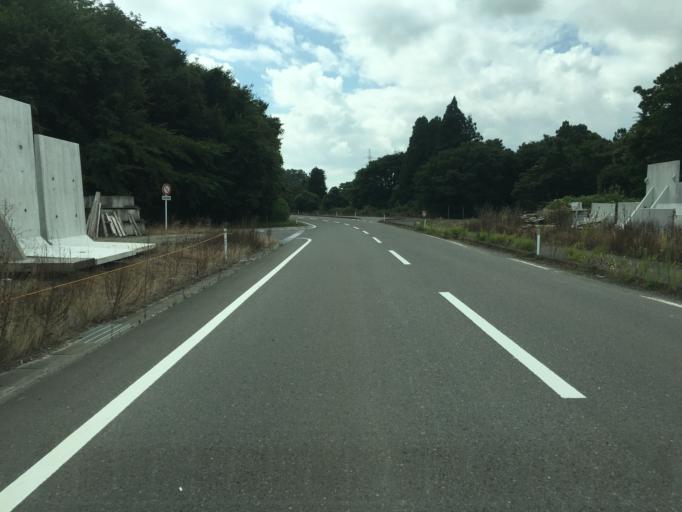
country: JP
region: Fukushima
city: Motomiya
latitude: 37.4780
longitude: 140.3371
